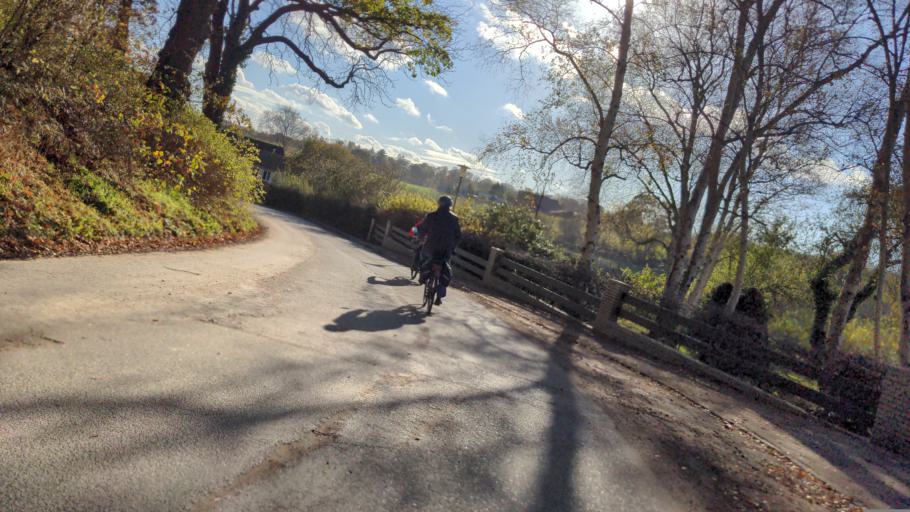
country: DE
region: Schleswig-Holstein
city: Ratekau
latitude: 53.9617
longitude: 10.7114
